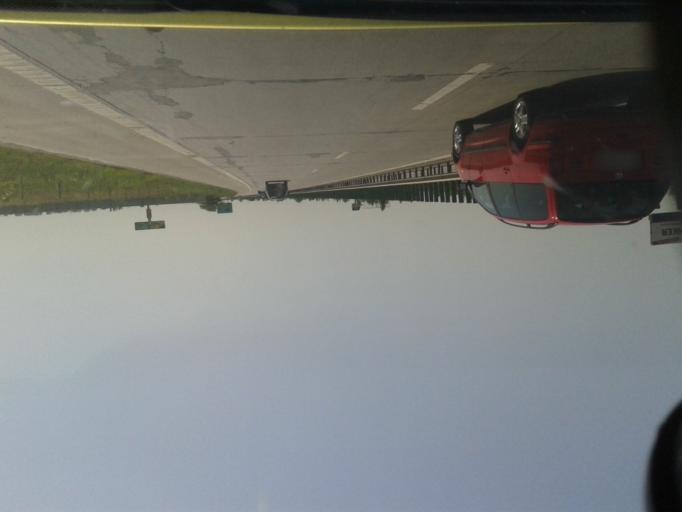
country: RO
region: Ilfov
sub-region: Comuna Cernica
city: Caldararu
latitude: 44.4091
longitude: 26.2467
